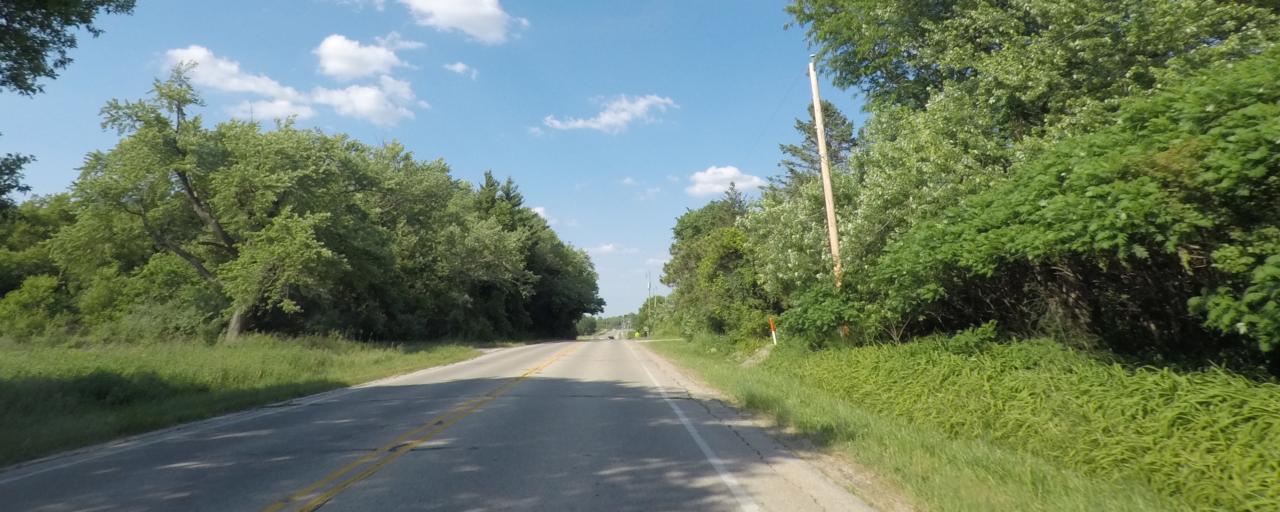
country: US
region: Wisconsin
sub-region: Waukesha County
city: Big Bend
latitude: 42.8554
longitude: -88.2464
